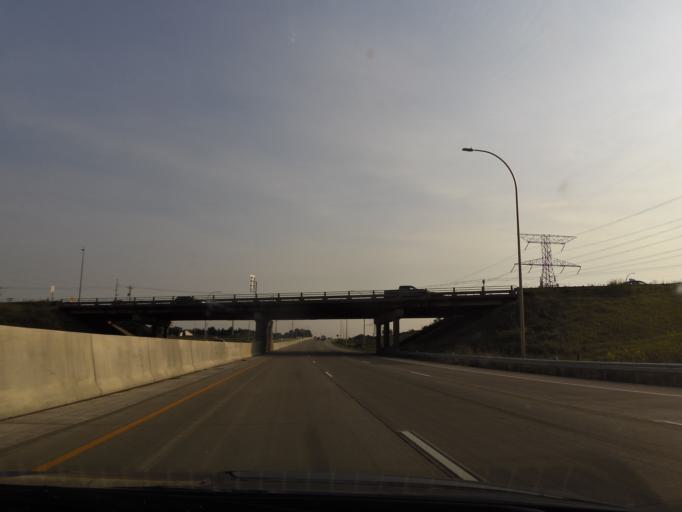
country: US
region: Minnesota
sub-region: Hennepin County
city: Plymouth
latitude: 45.0293
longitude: -93.4526
